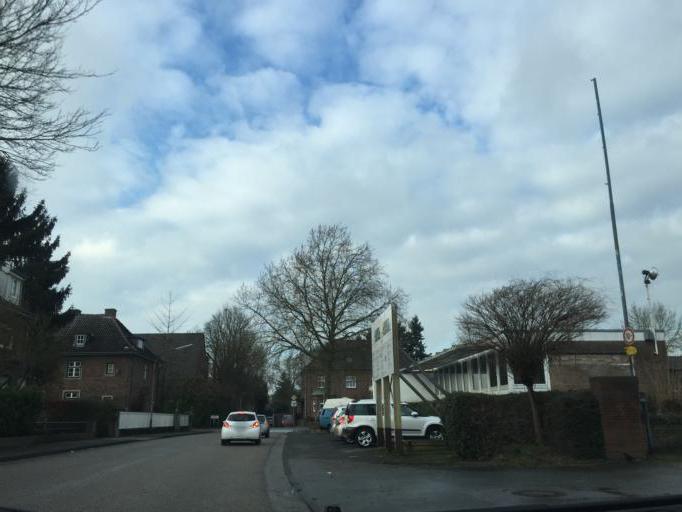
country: DE
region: North Rhine-Westphalia
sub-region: Regierungsbezirk Dusseldorf
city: Kleve
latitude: 51.7926
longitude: 6.1390
